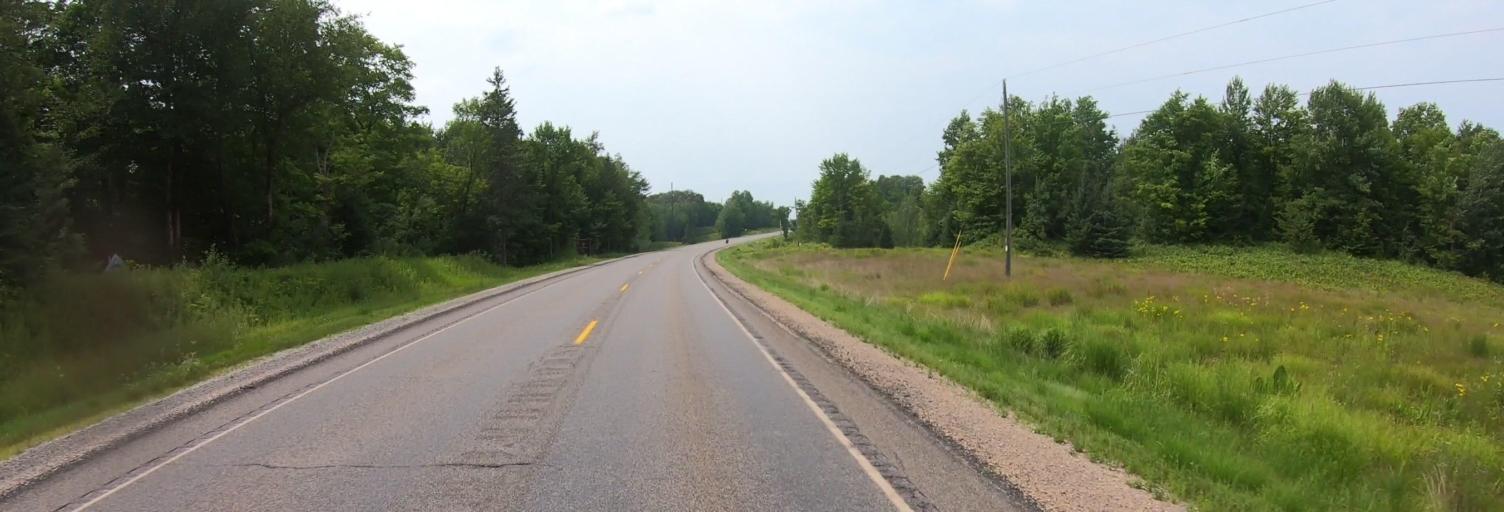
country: US
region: Michigan
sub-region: Alger County
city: Munising
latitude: 46.3320
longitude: -86.8625
